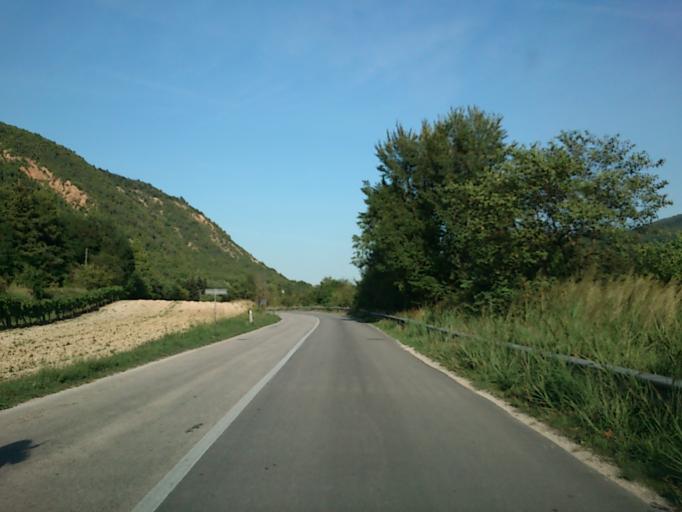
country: IT
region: The Marches
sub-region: Provincia di Pesaro e Urbino
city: Fossombrone
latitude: 43.6847
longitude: 12.7790
